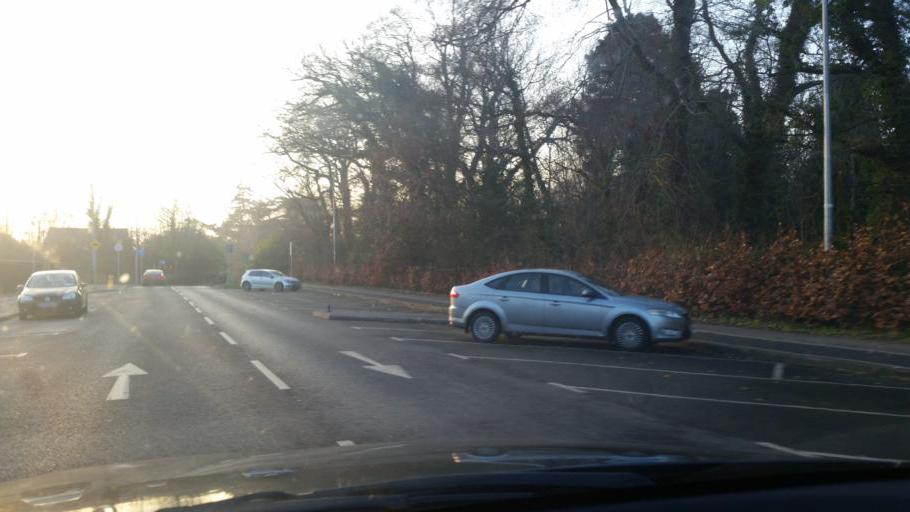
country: IE
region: Leinster
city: Hartstown
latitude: 53.3842
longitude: -6.4267
